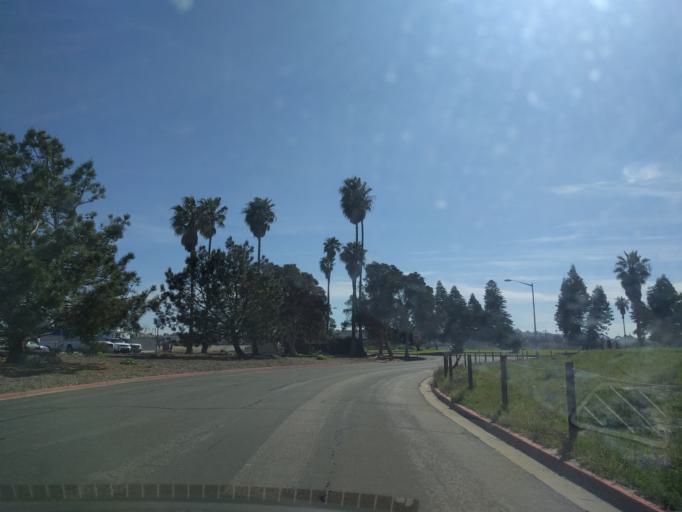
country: US
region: California
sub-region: San Diego County
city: La Jolla
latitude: 32.7598
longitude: -117.2412
